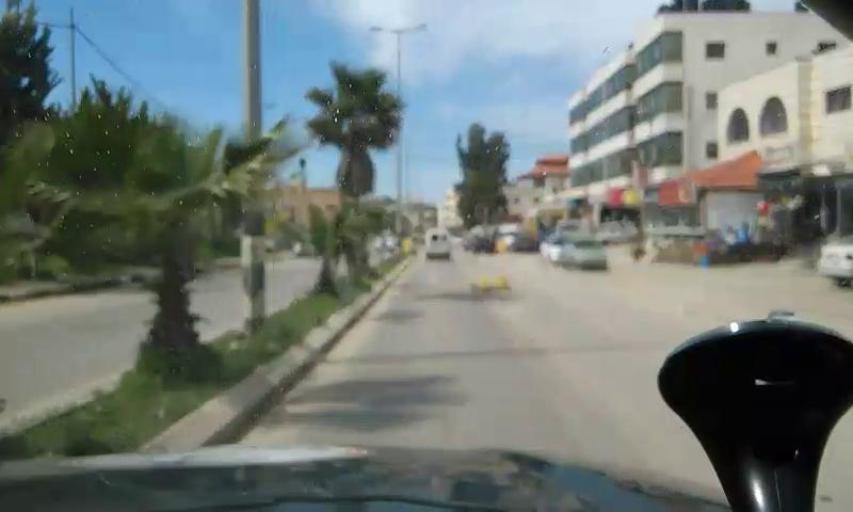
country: PS
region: West Bank
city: Al Judayrah
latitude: 31.8522
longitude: 35.1982
